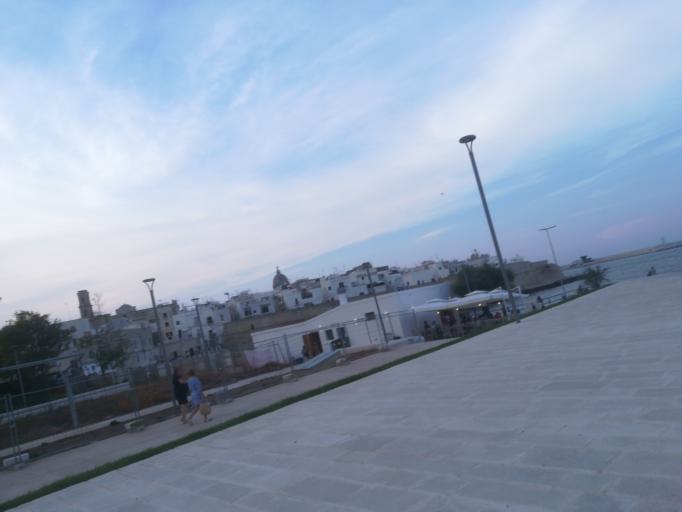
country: IT
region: Apulia
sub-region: Provincia di Bari
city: Monopoli
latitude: 40.9499
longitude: 17.3063
